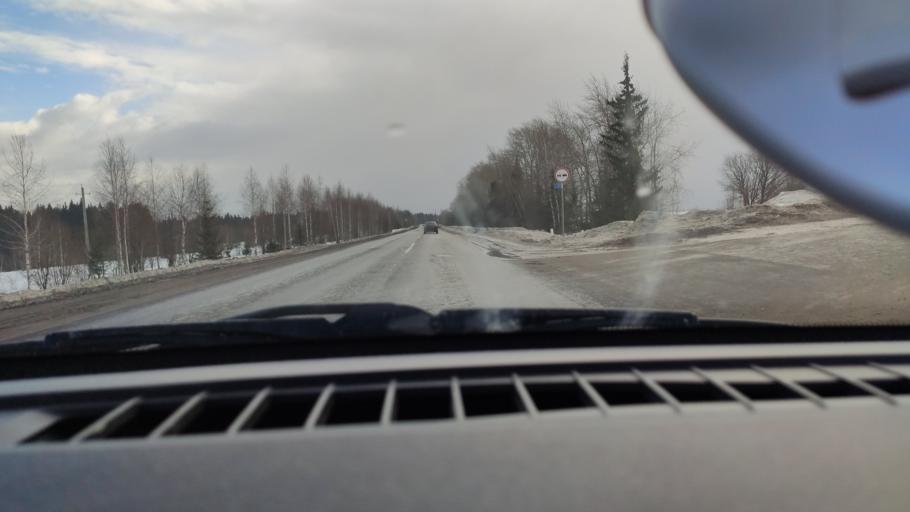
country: RU
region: Perm
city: Nytva
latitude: 57.9446
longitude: 55.3646
